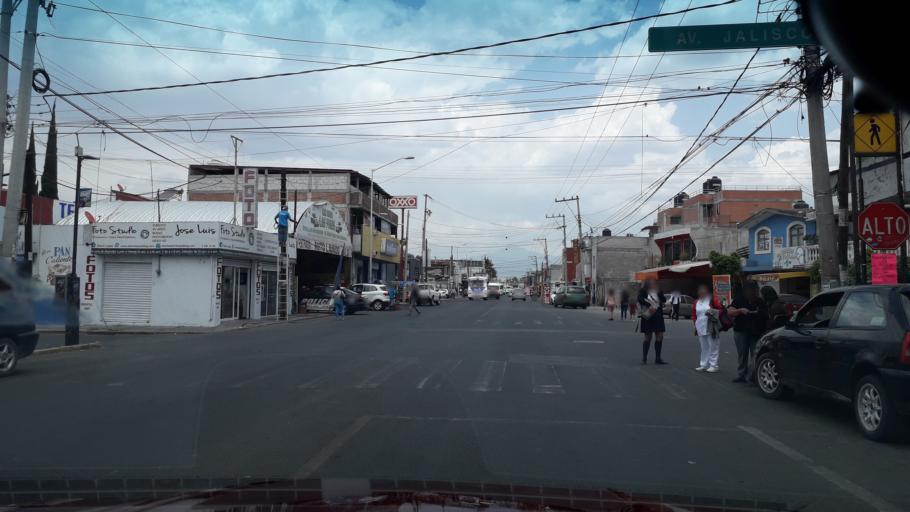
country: MX
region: Puebla
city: Tlazcalancingo
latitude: 19.0010
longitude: -98.2372
